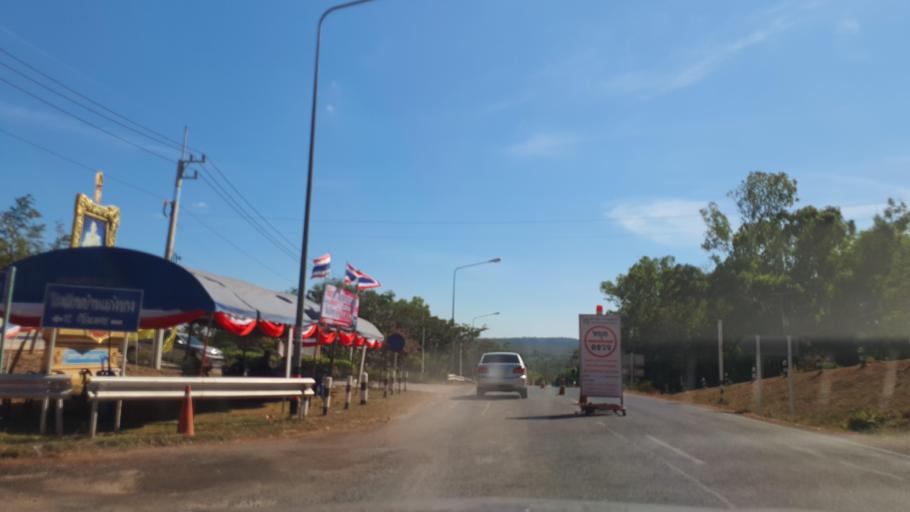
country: TH
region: Kalasin
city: Khao Wong
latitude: 16.7650
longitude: 104.1551
